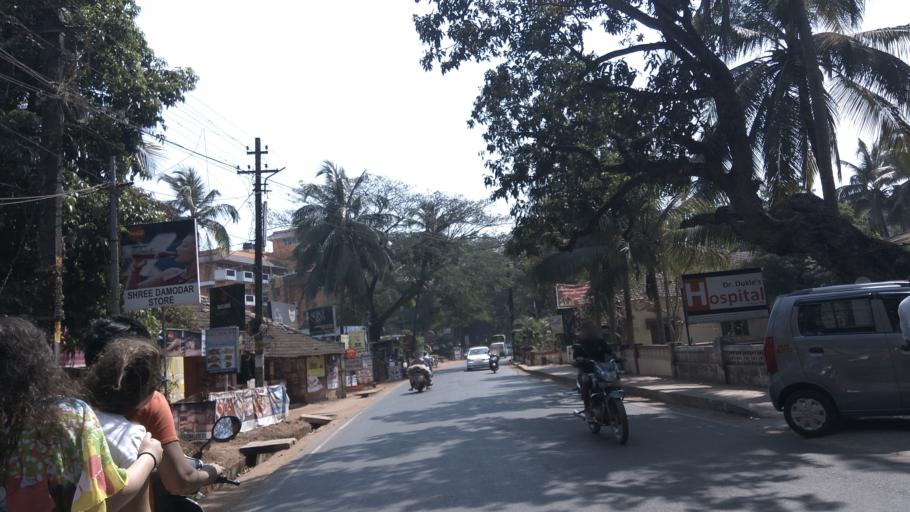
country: IN
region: Goa
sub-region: North Goa
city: Candolim
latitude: 15.5284
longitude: 73.7652
